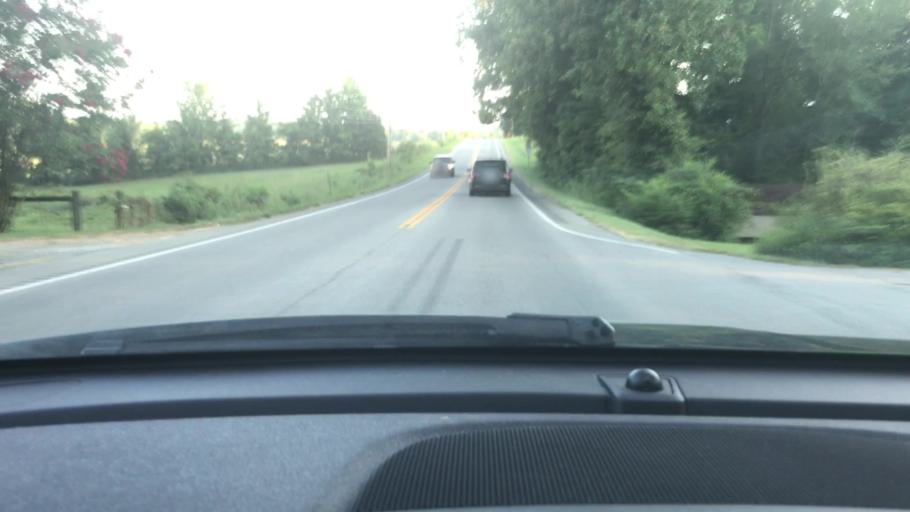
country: US
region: Tennessee
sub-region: Dickson County
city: Dickson
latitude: 36.0952
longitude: -87.3757
